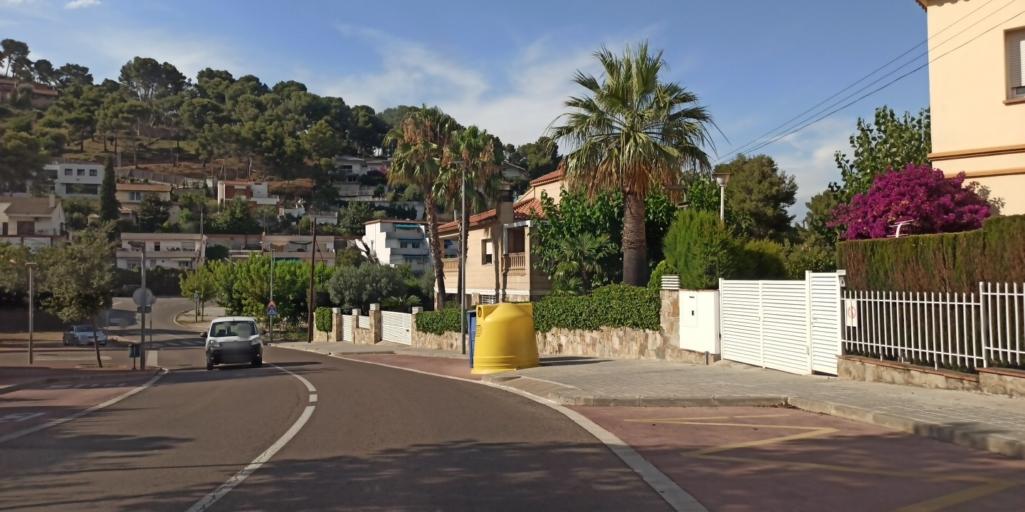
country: ES
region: Catalonia
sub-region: Provincia de Barcelona
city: Santa Coloma de Cervello
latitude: 41.3651
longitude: 2.0126
